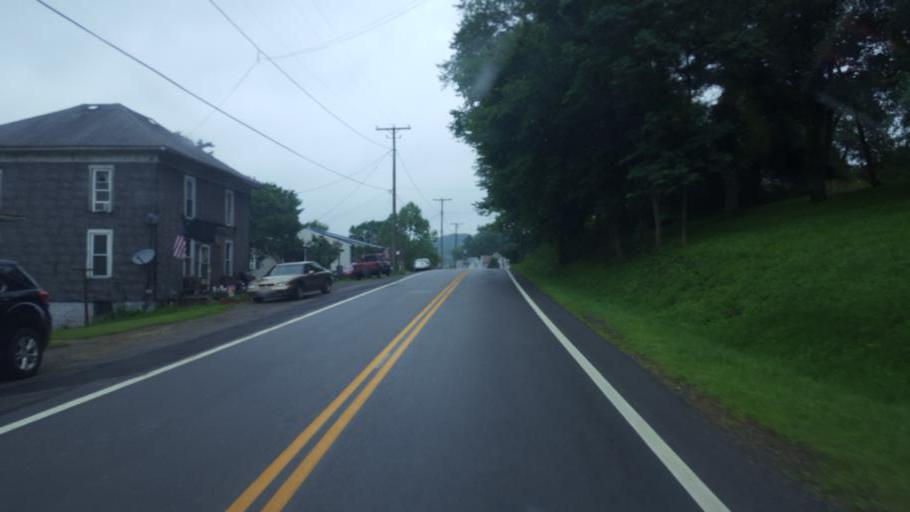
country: US
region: Ohio
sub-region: Columbiana County
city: Salineville
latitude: 40.5167
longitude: -80.8876
